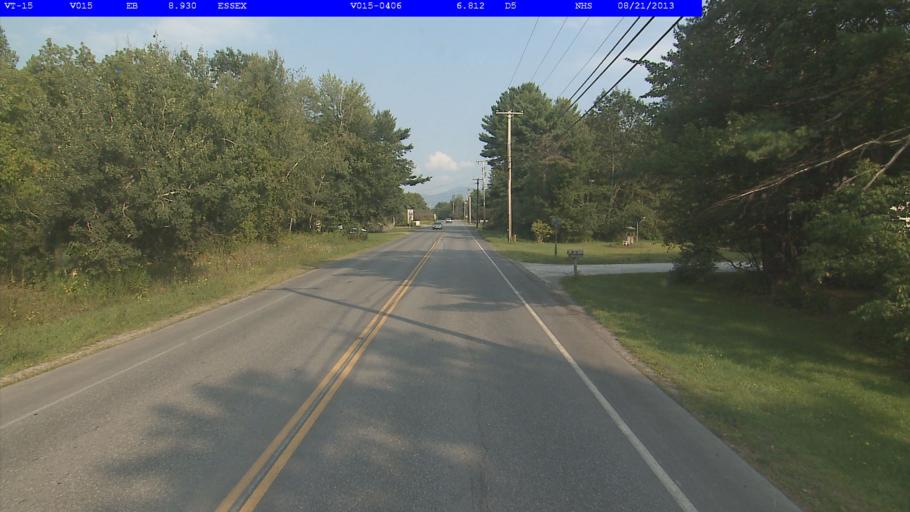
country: US
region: Vermont
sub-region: Chittenden County
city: Jericho
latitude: 44.5031
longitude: -73.0332
